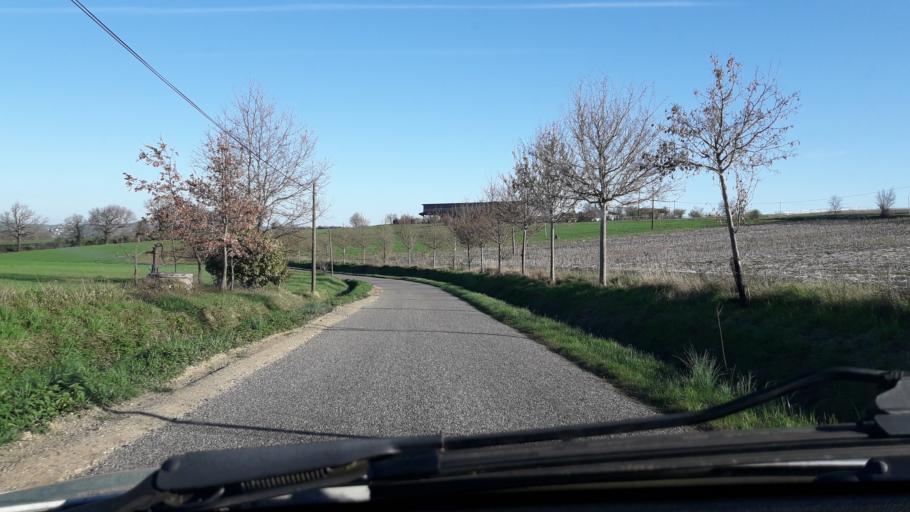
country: FR
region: Midi-Pyrenees
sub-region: Departement du Gers
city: Samatan
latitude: 43.5818
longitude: 1.0031
